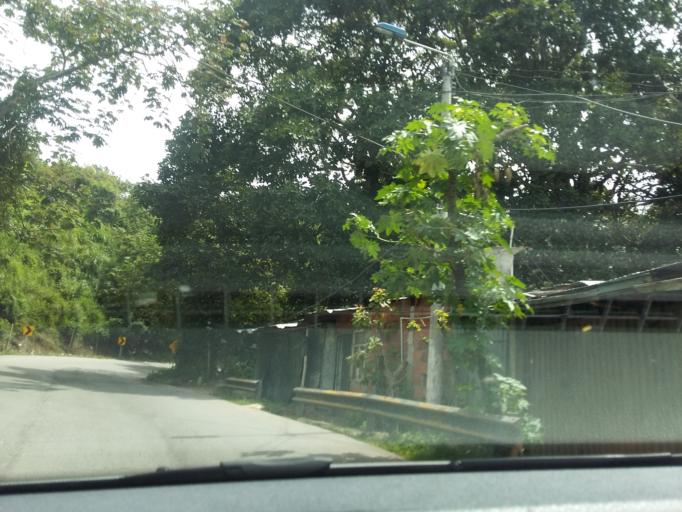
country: CO
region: Santander
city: Bucaramanga
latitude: 7.1283
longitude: -73.0978
